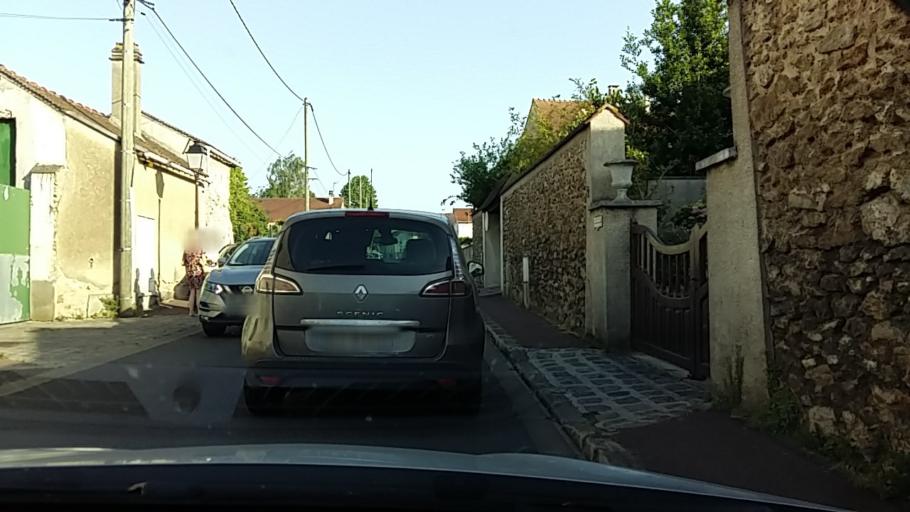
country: FR
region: Ile-de-France
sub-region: Departement du Val-de-Marne
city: Noiseau
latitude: 48.7782
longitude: 2.5485
